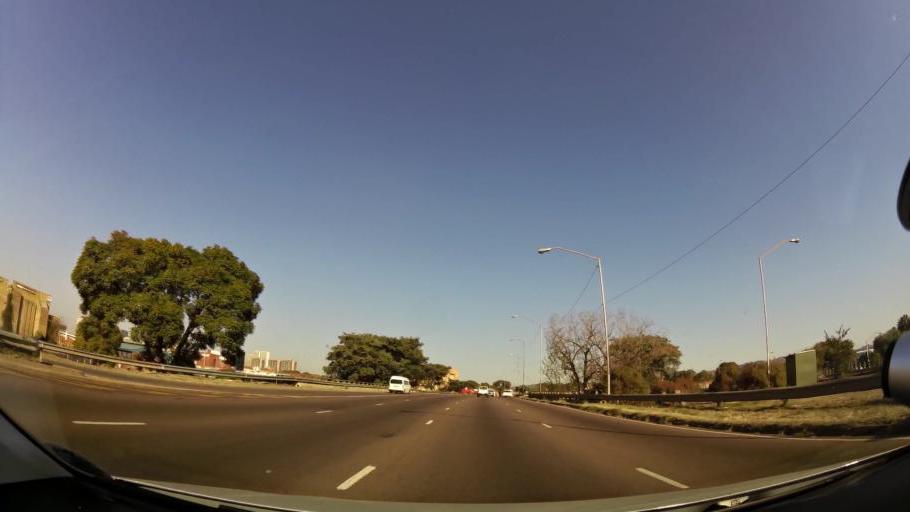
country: ZA
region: Gauteng
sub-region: City of Tshwane Metropolitan Municipality
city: Pretoria
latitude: -25.7376
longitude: 28.1718
